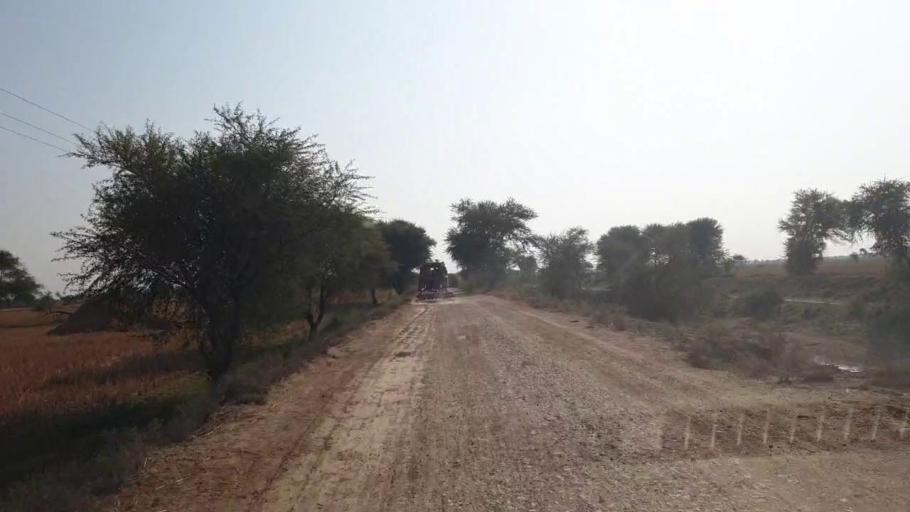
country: PK
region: Sindh
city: Kario
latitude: 24.9074
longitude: 68.6491
